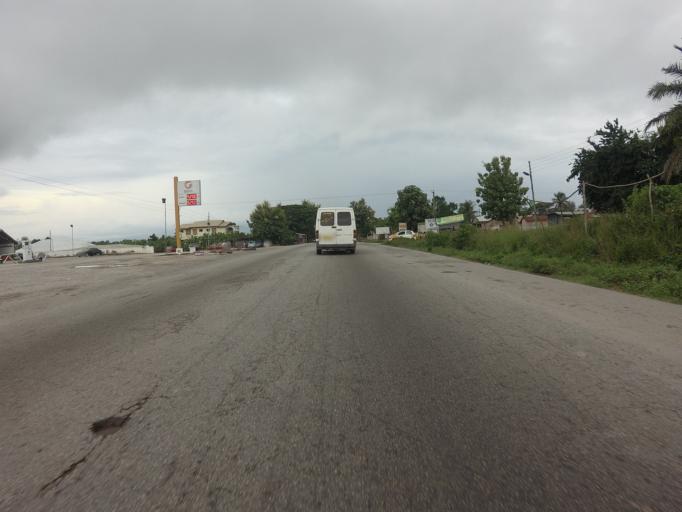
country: GH
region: Ashanti
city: Konongo
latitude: 6.6156
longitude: -1.1558
